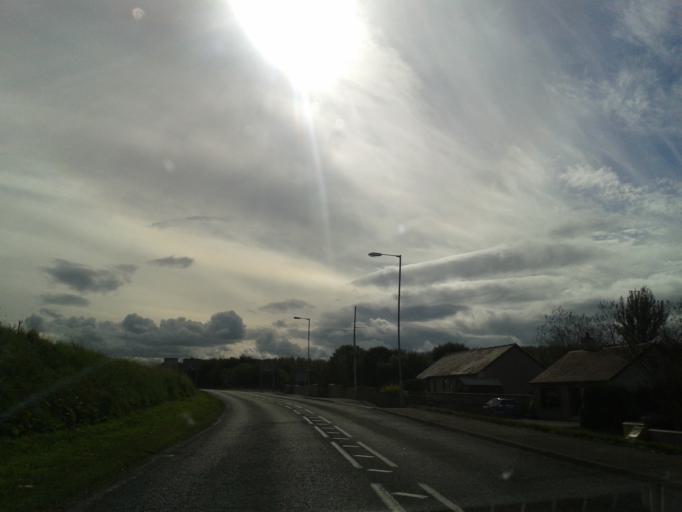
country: GB
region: Scotland
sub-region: Aberdeenshire
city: Portsoy
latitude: 57.6769
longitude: -2.6880
